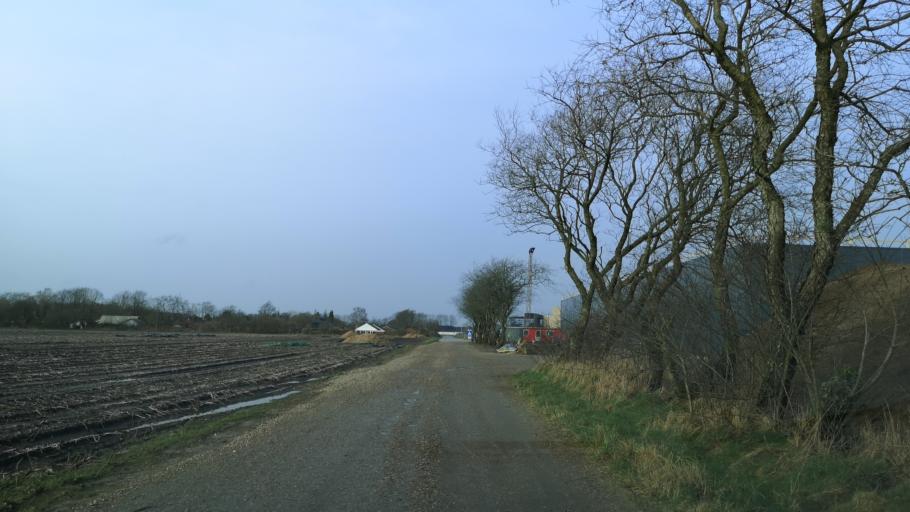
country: DK
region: Central Jutland
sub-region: Ikast-Brande Kommune
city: Brande
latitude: 56.0032
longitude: 9.1151
